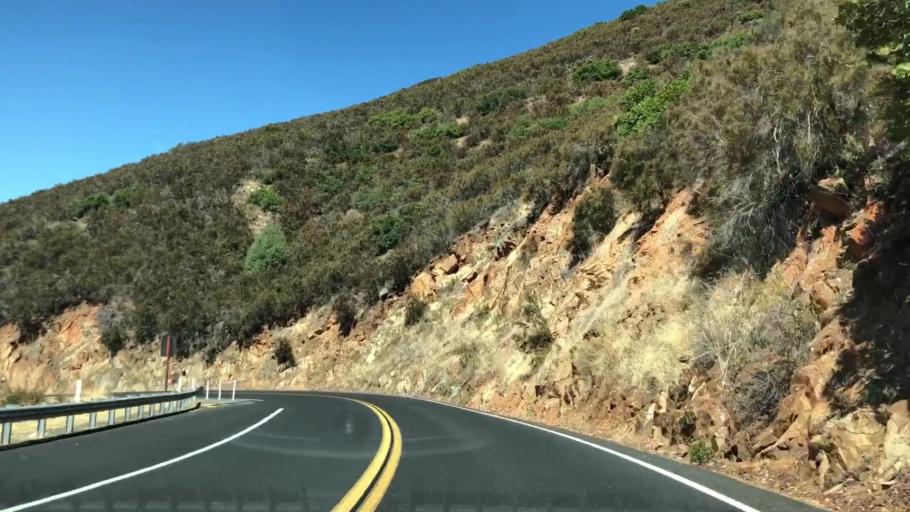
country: US
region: California
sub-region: Tuolumne County
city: Tuolumne City
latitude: 37.8215
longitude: -120.2844
